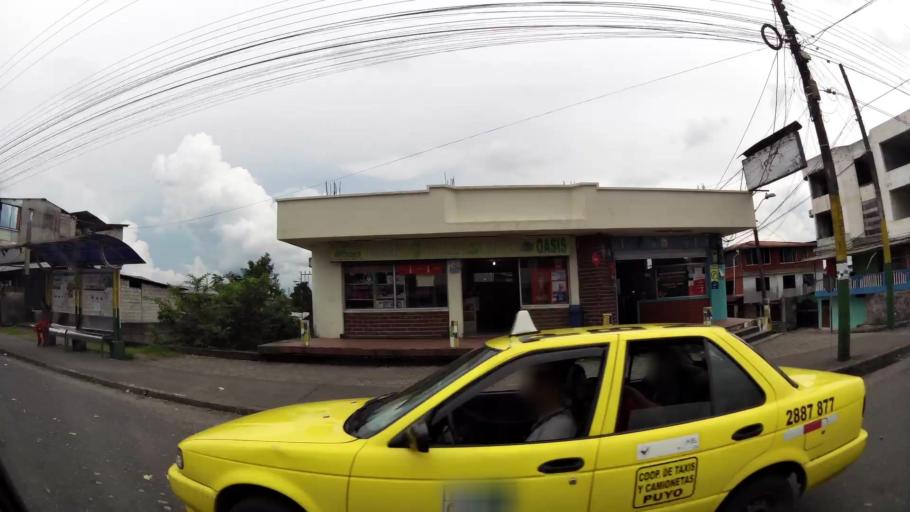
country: EC
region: Pastaza
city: Puyo
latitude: -1.4925
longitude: -78.0108
